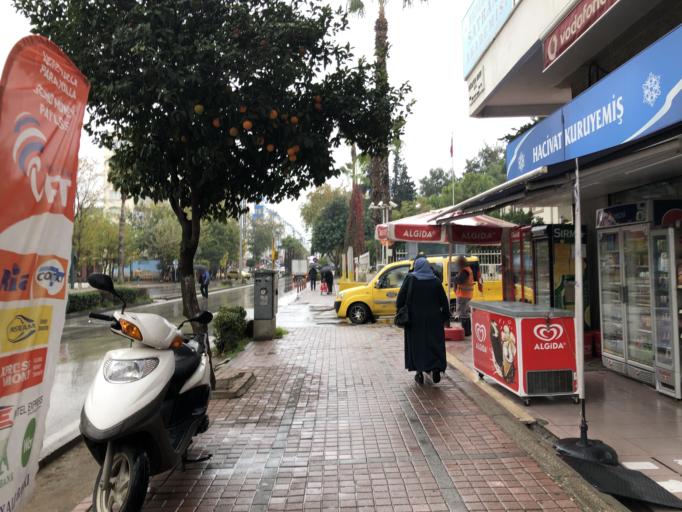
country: TR
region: Antalya
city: Antalya
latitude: 36.8924
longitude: 30.6941
